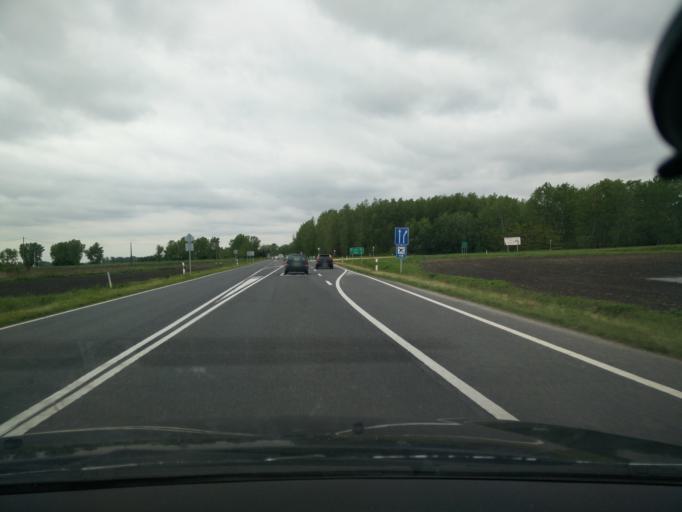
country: HU
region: Veszprem
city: Papa
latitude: 47.3512
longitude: 17.4543
